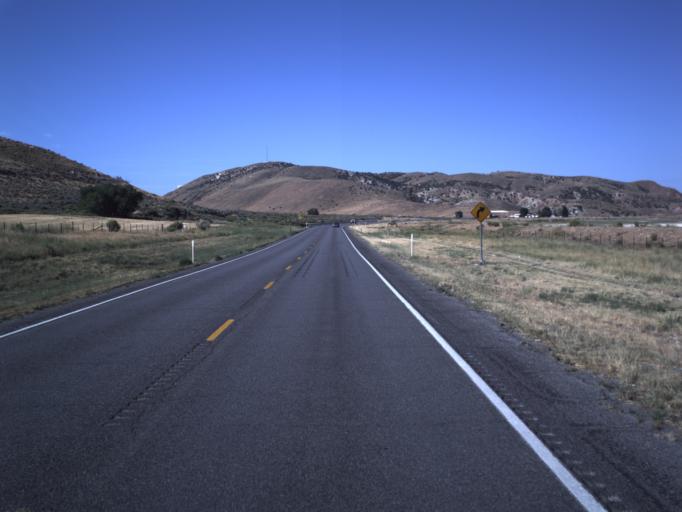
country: US
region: Utah
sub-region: Sanpete County
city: Manti
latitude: 39.1769
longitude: -111.7012
